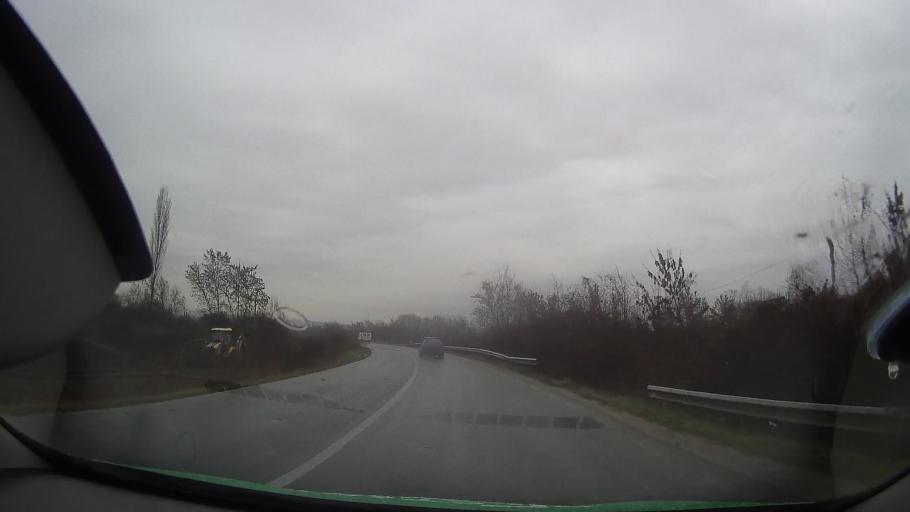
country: RO
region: Bihor
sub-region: Comuna Sambata
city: Sambata
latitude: 46.7900
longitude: 22.2043
